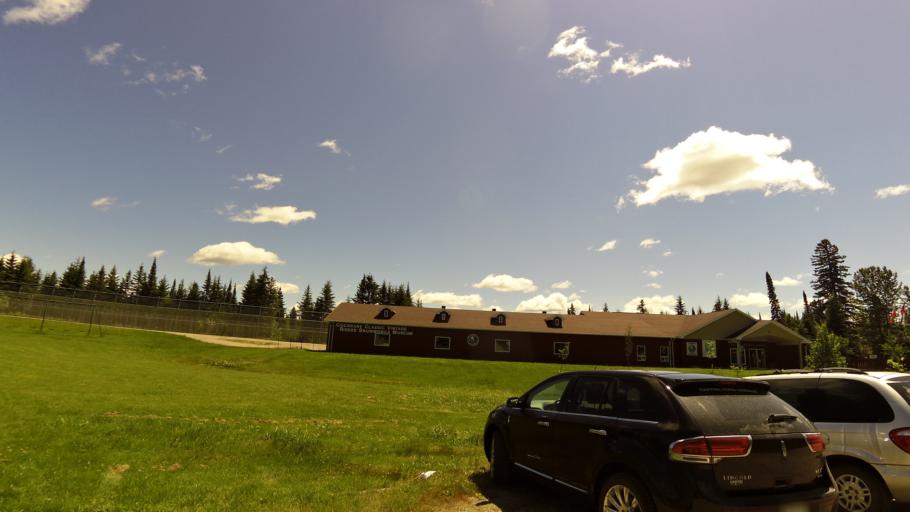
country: CA
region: Ontario
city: Iroquois Falls
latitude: 49.0543
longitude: -81.0174
